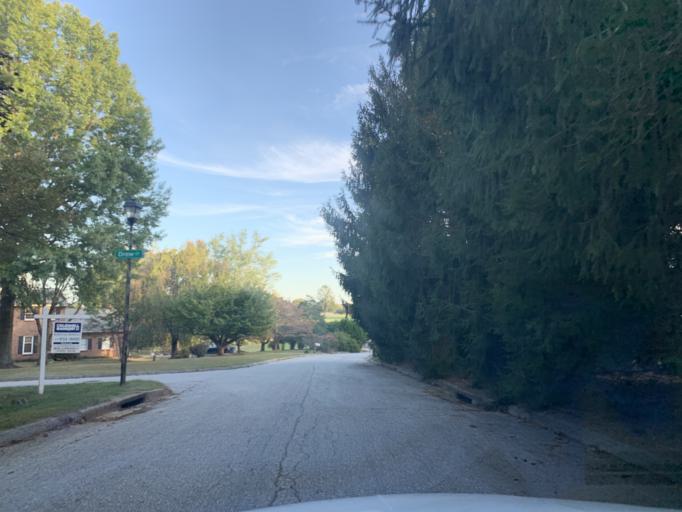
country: US
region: Maryland
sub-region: Harford County
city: Fallston
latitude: 39.4896
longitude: -76.4415
